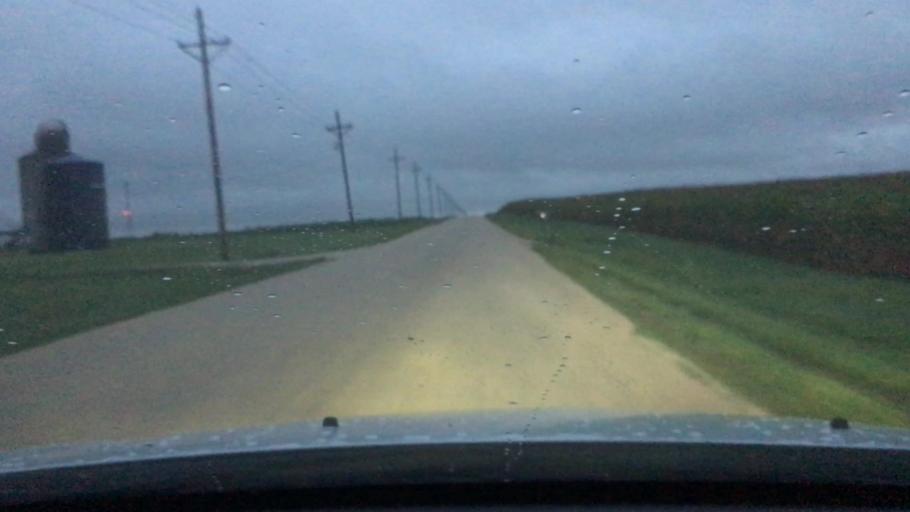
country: US
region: Illinois
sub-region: Ogle County
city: Rochelle
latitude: 41.8987
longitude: -88.9751
